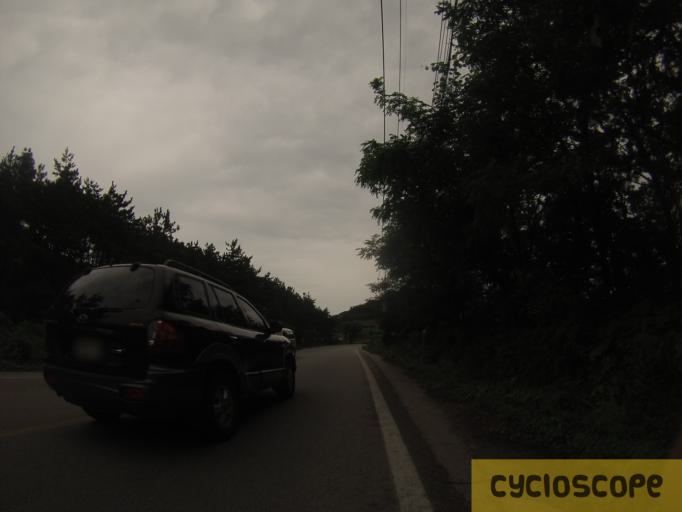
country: KR
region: Jeollabuk-do
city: Puan
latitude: 35.7526
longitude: 126.7445
